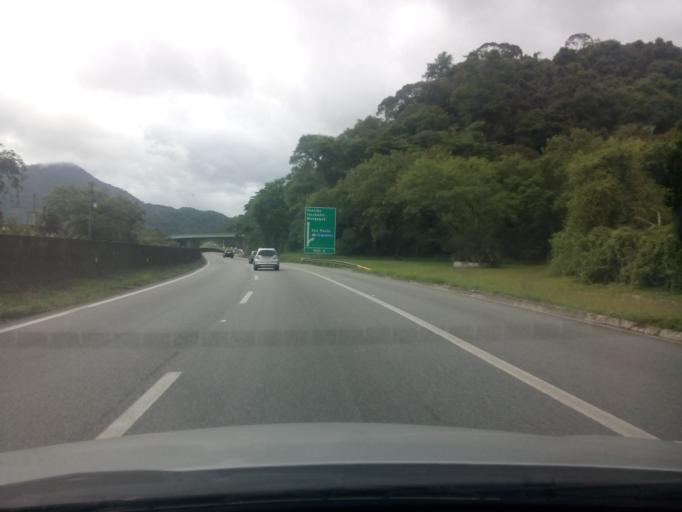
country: BR
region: Sao Paulo
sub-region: Cubatao
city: Cubatao
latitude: -23.8981
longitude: -46.4491
